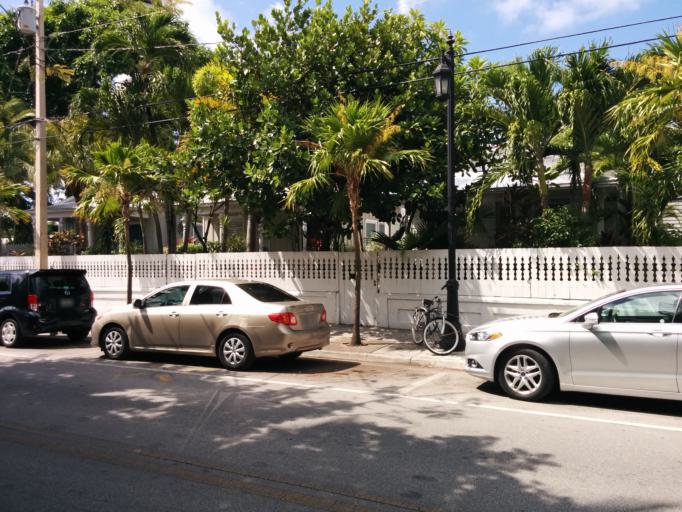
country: US
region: Florida
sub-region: Monroe County
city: Key West
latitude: 24.5511
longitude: -81.8009
